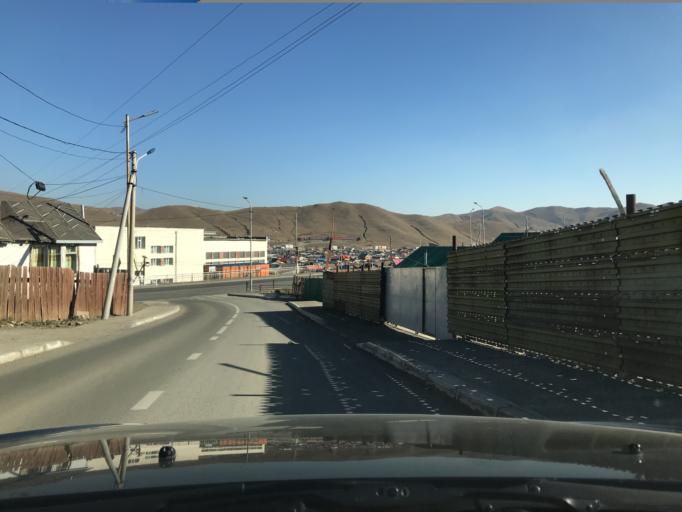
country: MN
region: Ulaanbaatar
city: Ulaanbaatar
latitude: 47.9952
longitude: 106.9248
